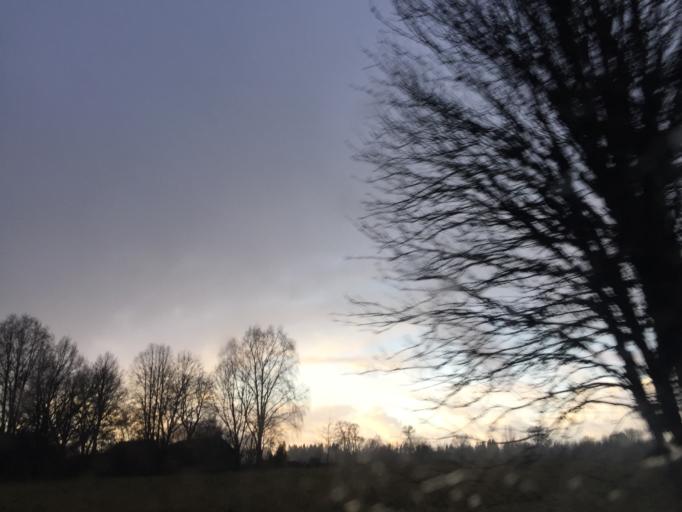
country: LV
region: Burtnieki
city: Matisi
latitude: 57.6867
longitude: 25.2496
